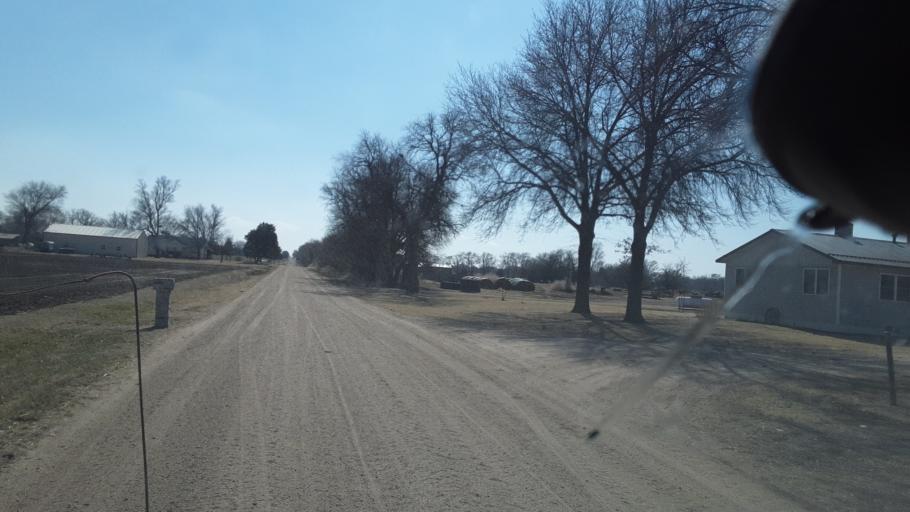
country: US
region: Kansas
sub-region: Reno County
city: Haven
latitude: 37.9153
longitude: -97.8484
